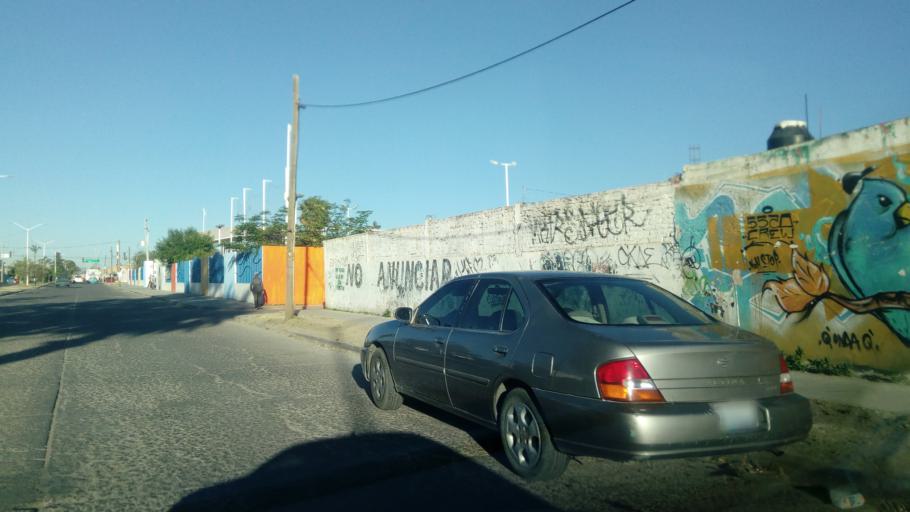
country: MX
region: Durango
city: Victoria de Durango
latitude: 24.0551
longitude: -104.5949
